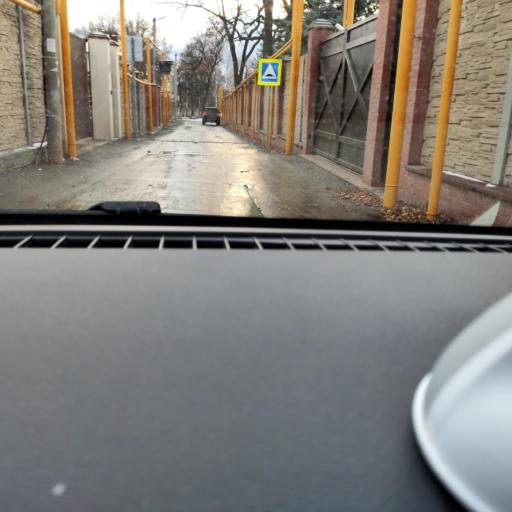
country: RU
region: Samara
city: Samara
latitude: 53.2385
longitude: 50.1729
